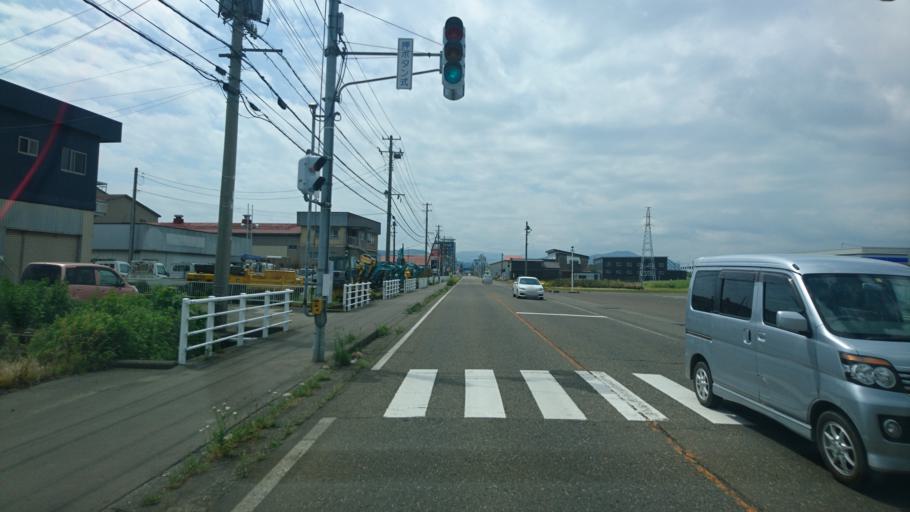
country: JP
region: Niigata
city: Arai
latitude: 37.0666
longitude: 138.2581
